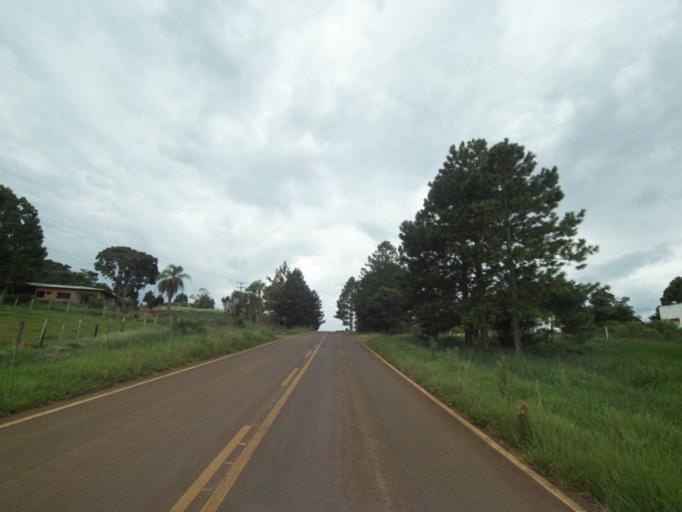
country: BR
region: Parana
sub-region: Pitanga
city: Pitanga
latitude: -24.8950
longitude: -51.9630
